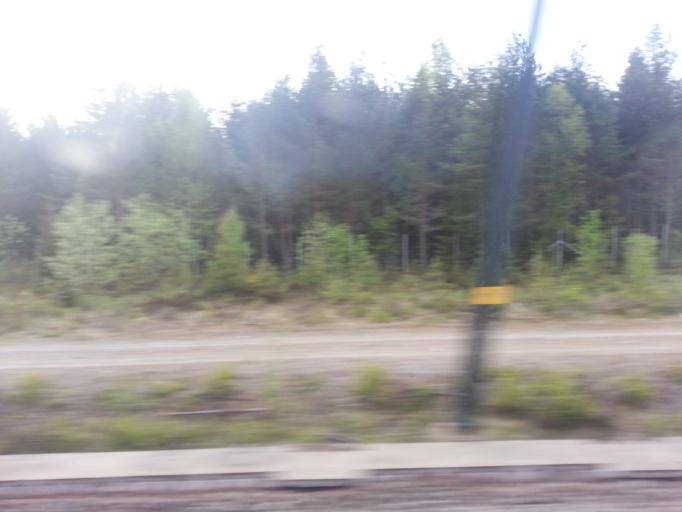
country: NO
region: Akershus
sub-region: Eidsvoll
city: Raholt
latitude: 60.2446
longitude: 11.1175
